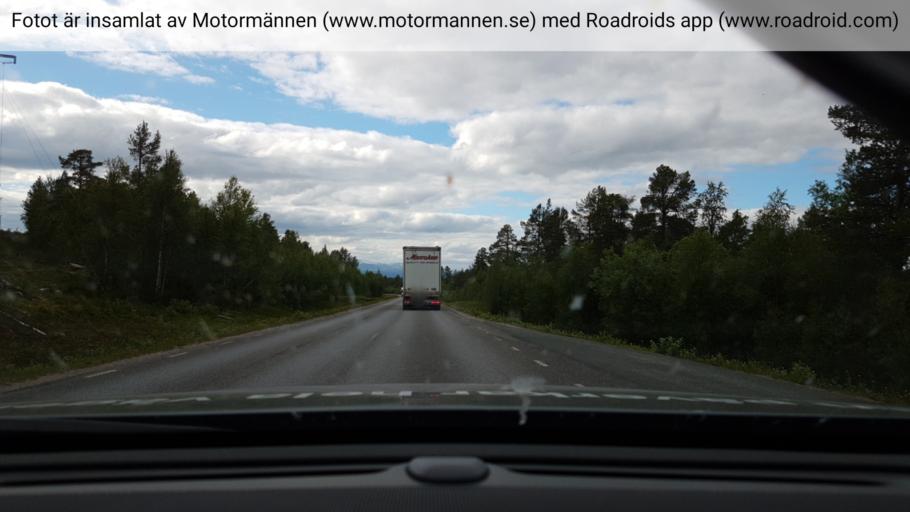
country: SE
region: Norrbotten
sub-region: Arjeplogs Kommun
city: Arjeplog
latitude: 66.3593
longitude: 17.0475
